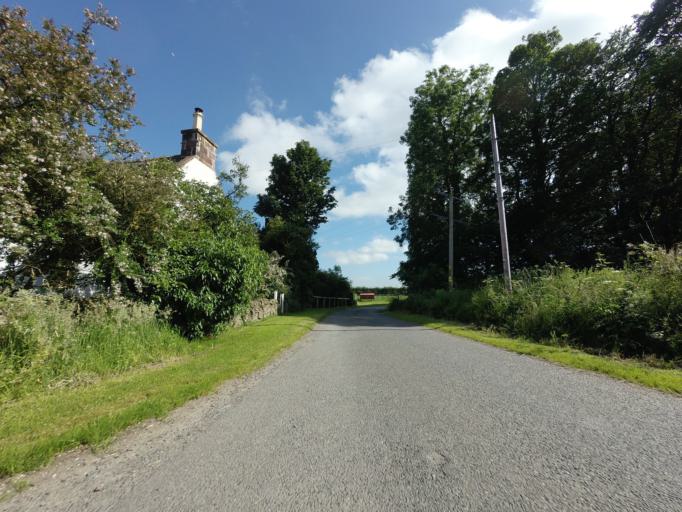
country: GB
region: Scotland
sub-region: Aberdeenshire
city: Turriff
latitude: 57.5889
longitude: -2.5042
